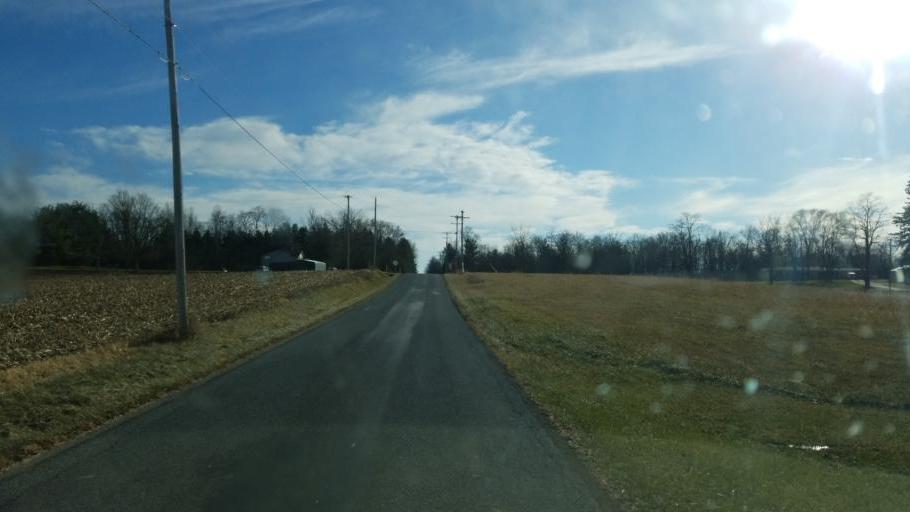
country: US
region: Ohio
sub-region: Crawford County
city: Crestline
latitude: 40.7195
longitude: -82.6891
